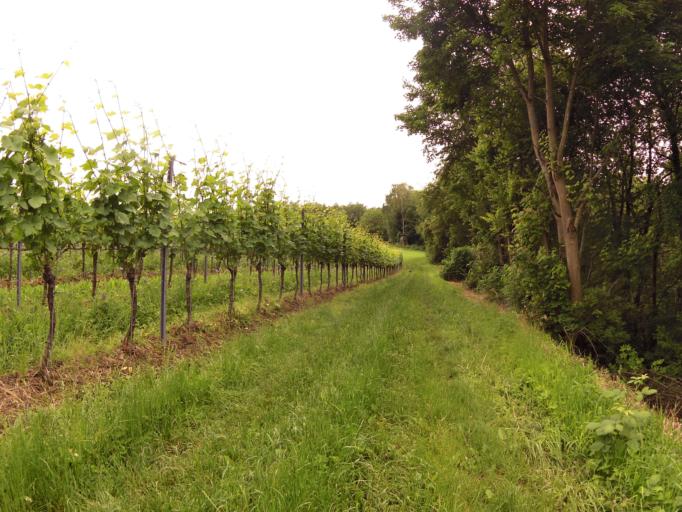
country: DE
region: Baden-Wuerttemberg
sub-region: Freiburg Region
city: Lahr
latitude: 48.3546
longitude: 7.8606
